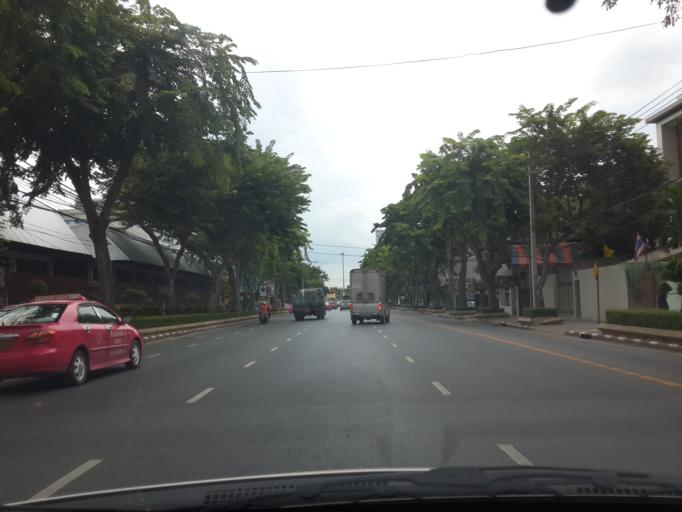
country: TH
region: Bangkok
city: Pom Prap Sattru Phai
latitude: 13.7564
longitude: 100.5086
